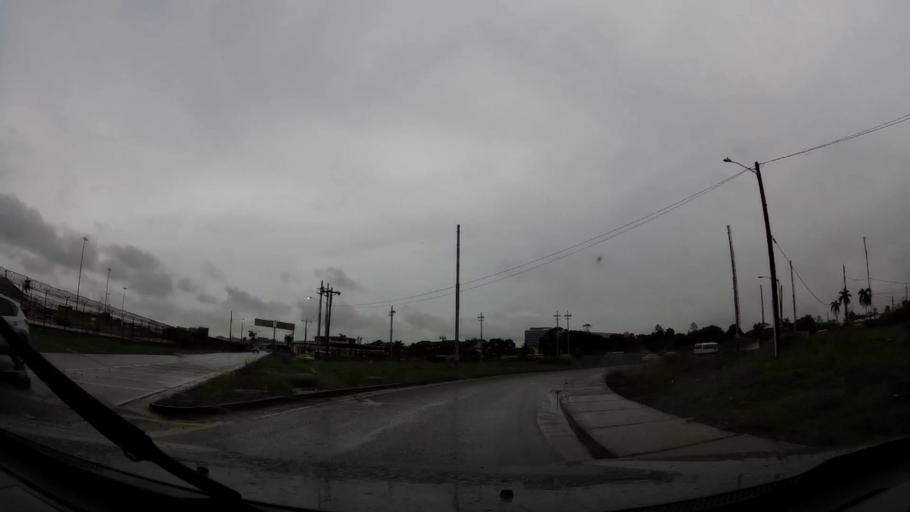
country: PA
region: Colon
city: Arco Iris
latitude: 9.3403
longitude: -79.8975
